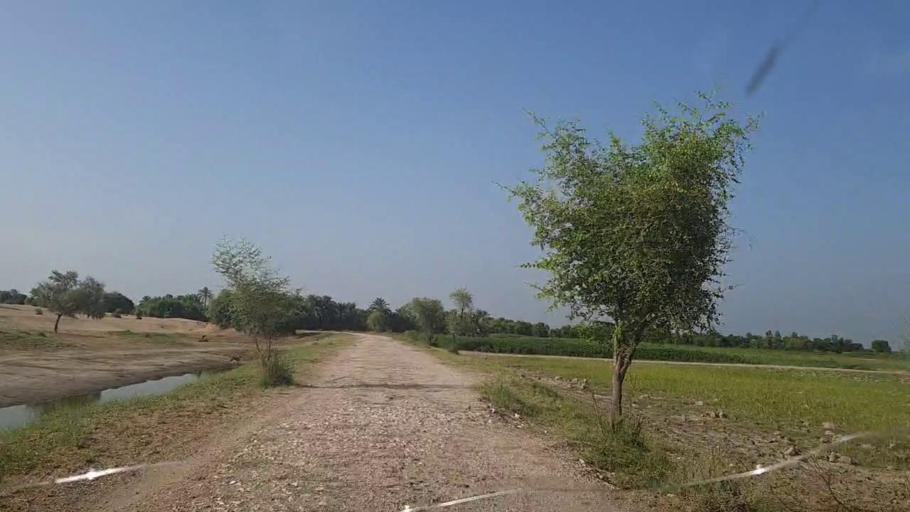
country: PK
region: Sindh
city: Khanpur
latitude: 27.7226
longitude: 69.3318
